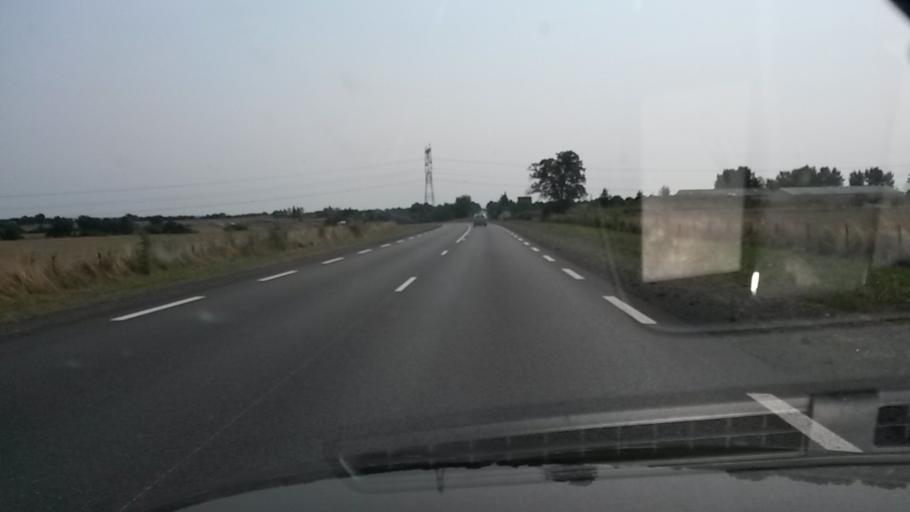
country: FR
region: Pays de la Loire
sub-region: Departement de la Loire-Atlantique
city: Mesanger
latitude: 47.4267
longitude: -1.1870
